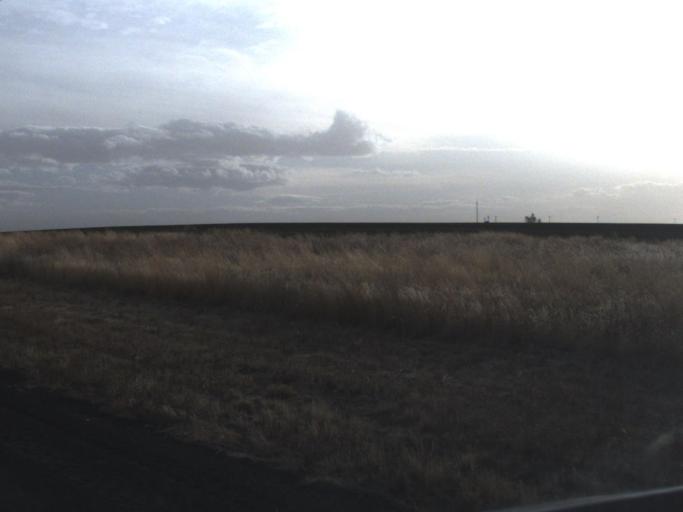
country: US
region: Washington
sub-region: Adams County
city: Ritzville
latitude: 47.1507
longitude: -118.6867
